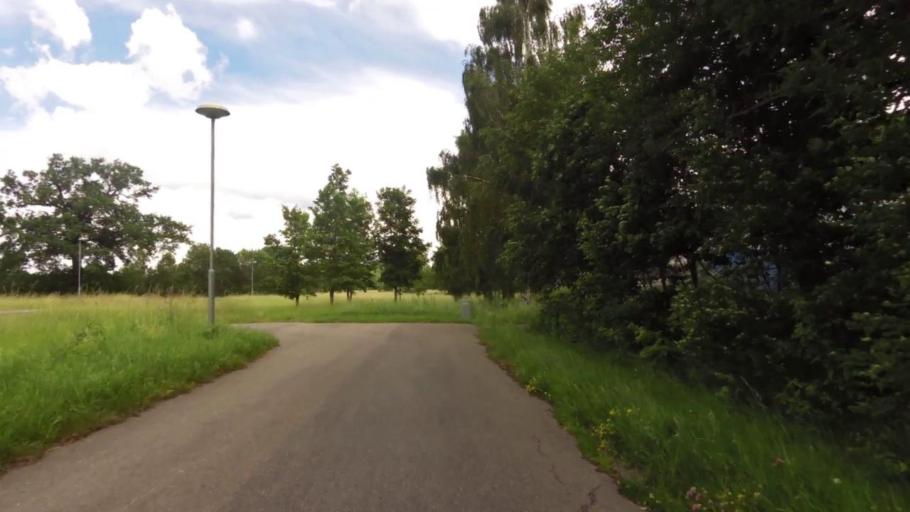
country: SE
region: OEstergoetland
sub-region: Linkopings Kommun
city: Malmslatt
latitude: 58.4030
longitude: 15.5576
